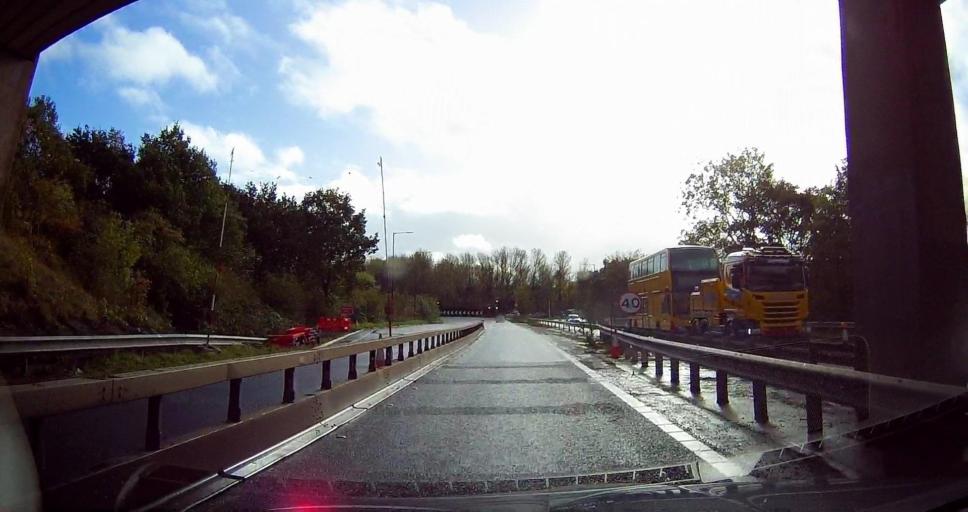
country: GB
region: England
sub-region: Warwickshire
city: Curdworth
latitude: 52.5329
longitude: -1.7768
